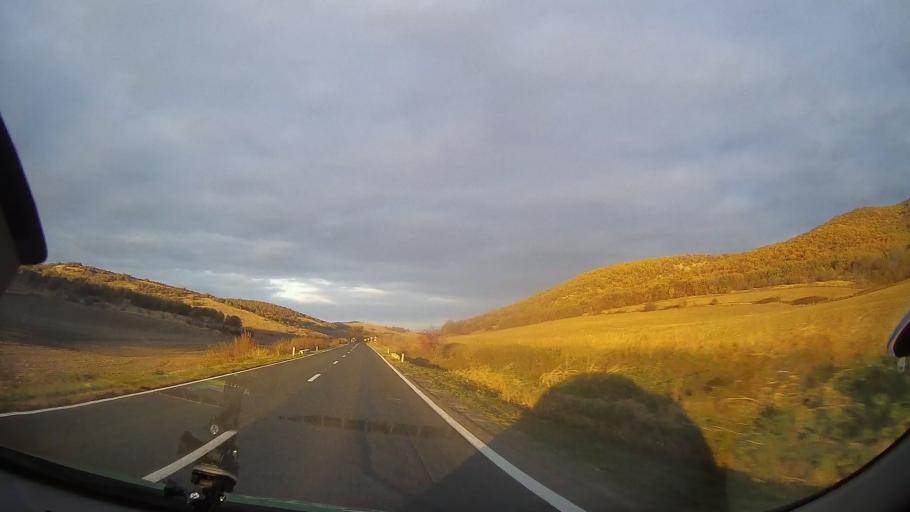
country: RO
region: Tulcea
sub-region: Comuna Ciucurova
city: Ciucurova
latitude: 44.9554
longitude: 28.5150
